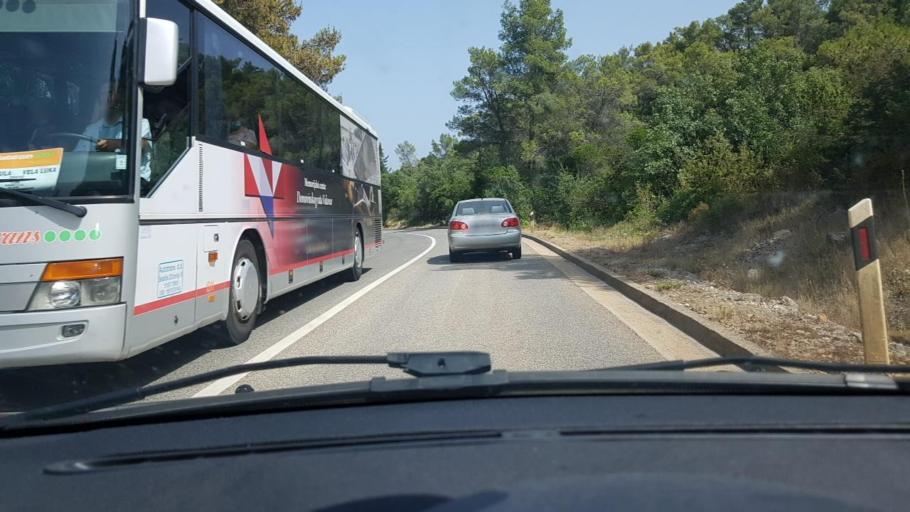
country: HR
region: Dubrovacko-Neretvanska
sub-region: Grad Korcula
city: Zrnovo
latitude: 42.9380
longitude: 17.0939
